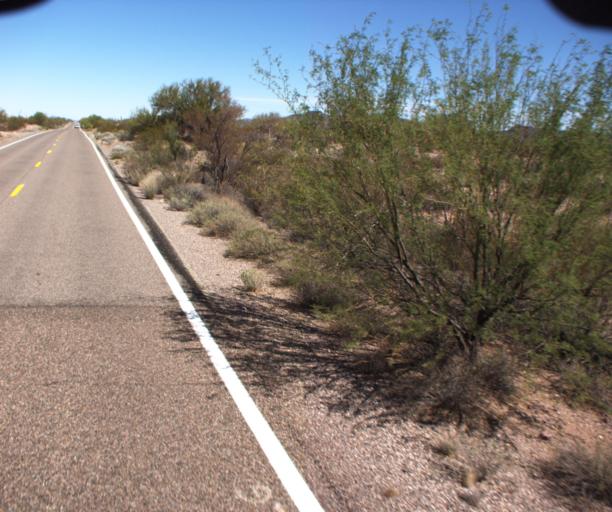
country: US
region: Arizona
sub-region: Pima County
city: Ajo
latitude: 32.1512
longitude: -112.7652
